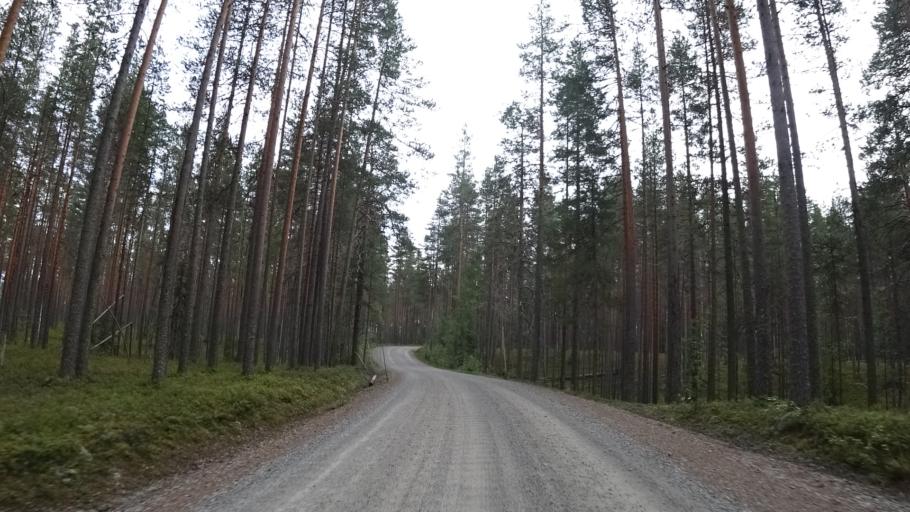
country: FI
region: North Karelia
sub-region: Joensuu
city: Ilomantsi
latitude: 62.6012
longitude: 31.1864
